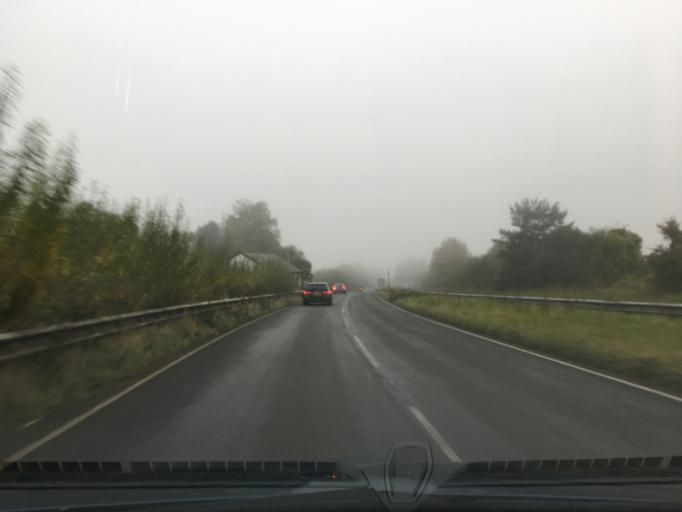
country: GB
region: England
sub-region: Hampshire
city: Four Marks
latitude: 51.1008
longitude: -1.0694
